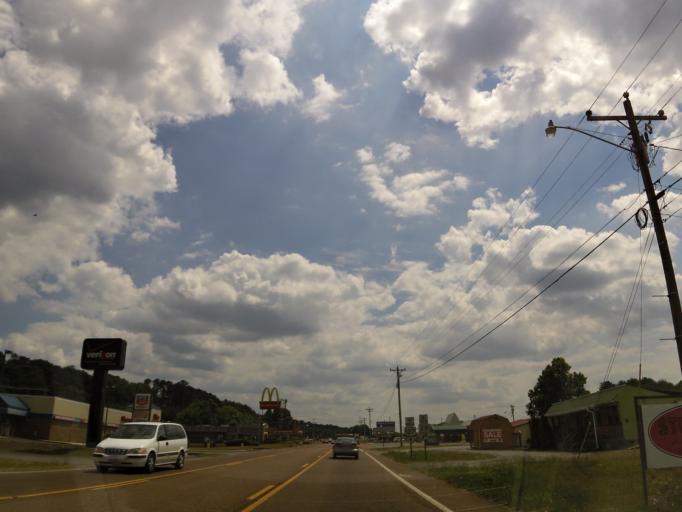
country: US
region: Tennessee
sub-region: Sequatchie County
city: Dunlap
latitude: 35.3637
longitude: -85.3941
